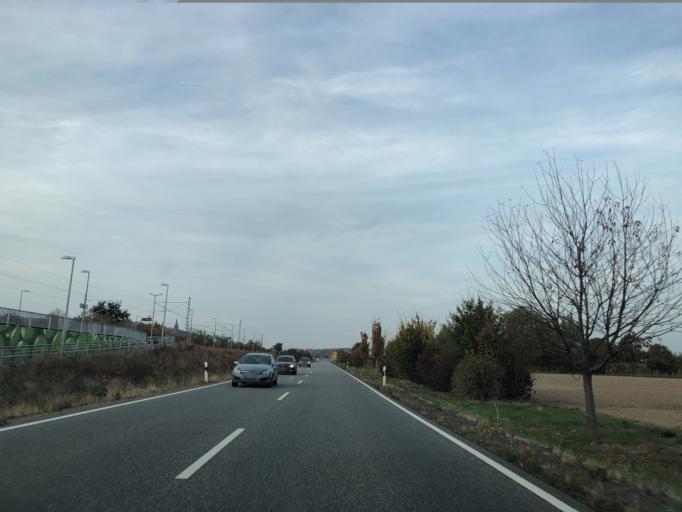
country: DE
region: Rheinland-Pfalz
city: Dienheim
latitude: 49.8404
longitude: 8.3573
